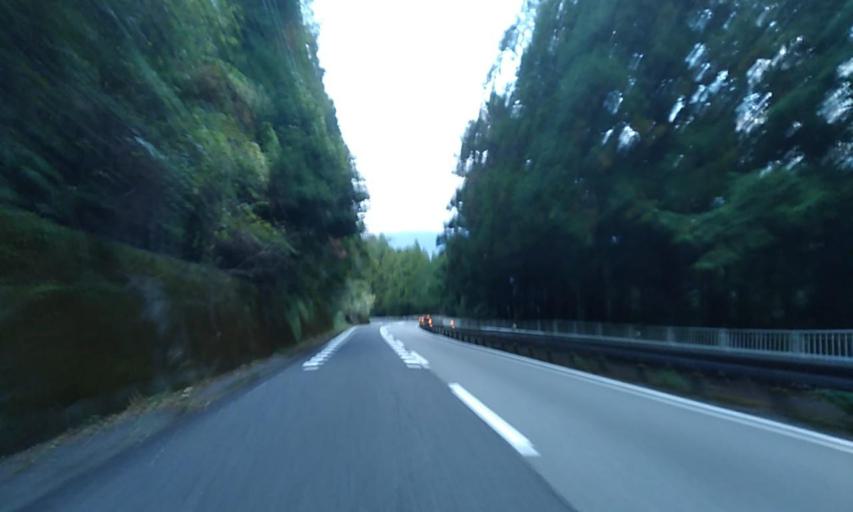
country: JP
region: Wakayama
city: Shingu
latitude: 33.7375
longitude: 135.9396
